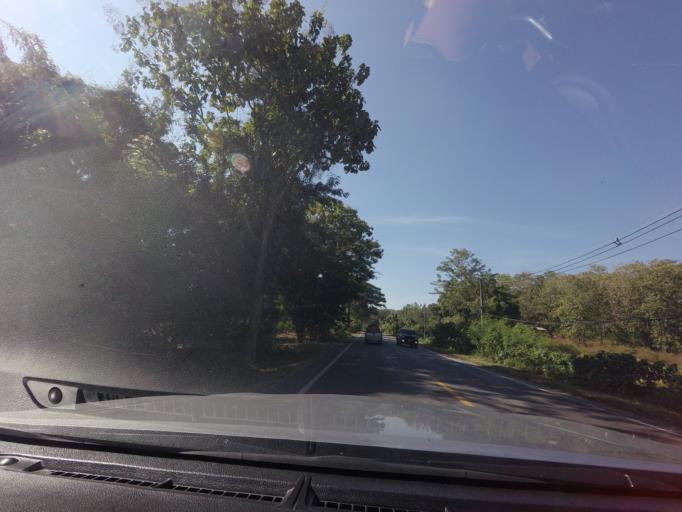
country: TH
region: Sukhothai
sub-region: Amphoe Si Satchanalai
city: Si Satchanalai
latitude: 17.6068
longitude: 99.7098
